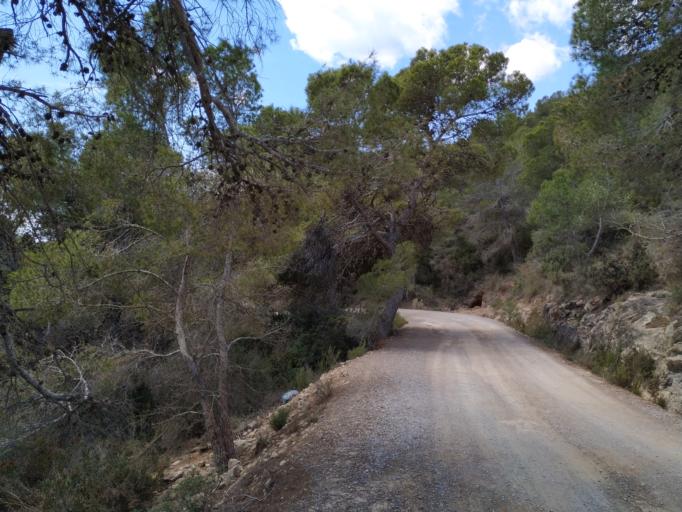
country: ES
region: Balearic Islands
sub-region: Illes Balears
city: Ibiza
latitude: 38.9227
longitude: 1.4752
